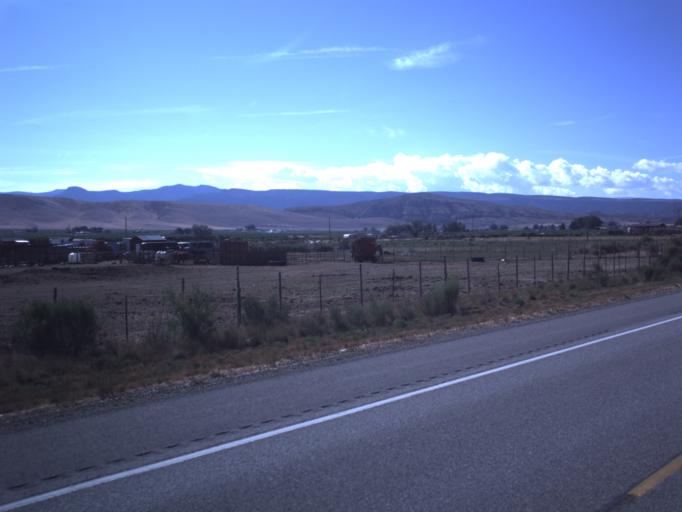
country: US
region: Utah
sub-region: Sanpete County
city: Centerfield
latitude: 39.0729
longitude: -111.8209
